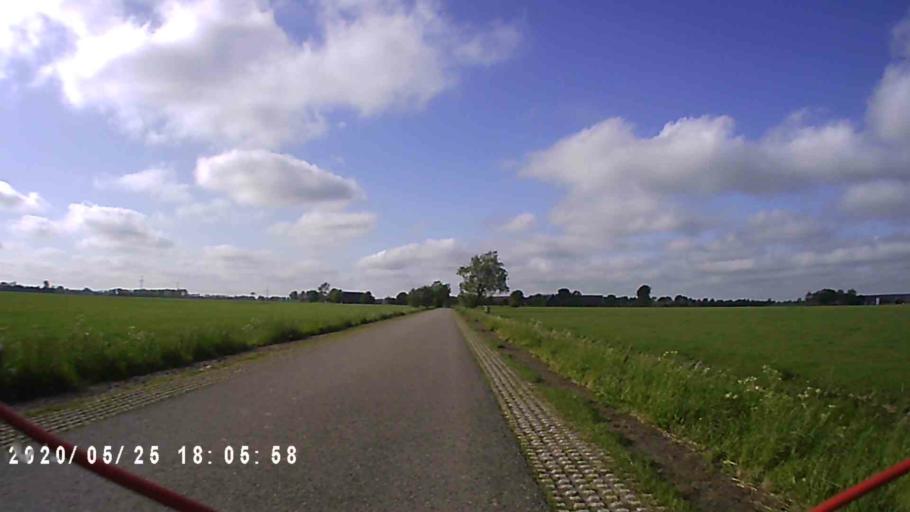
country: NL
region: Groningen
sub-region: Gemeente Winsum
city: Winsum
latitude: 53.2945
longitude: 6.4926
